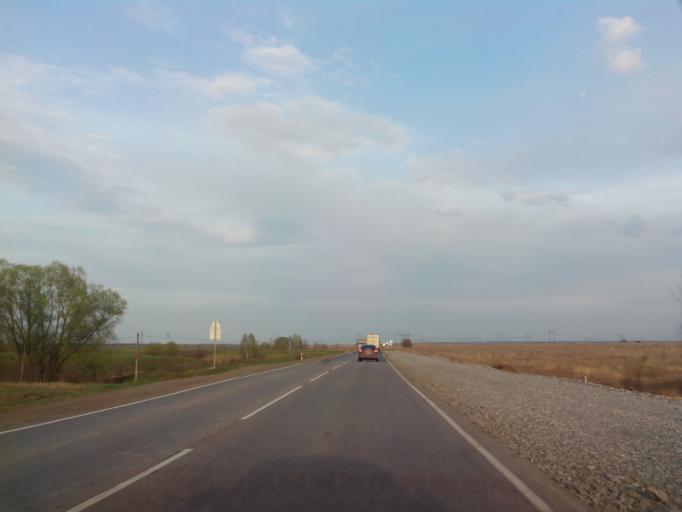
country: RU
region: Rjazan
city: Korablino
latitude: 53.7507
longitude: 39.8487
